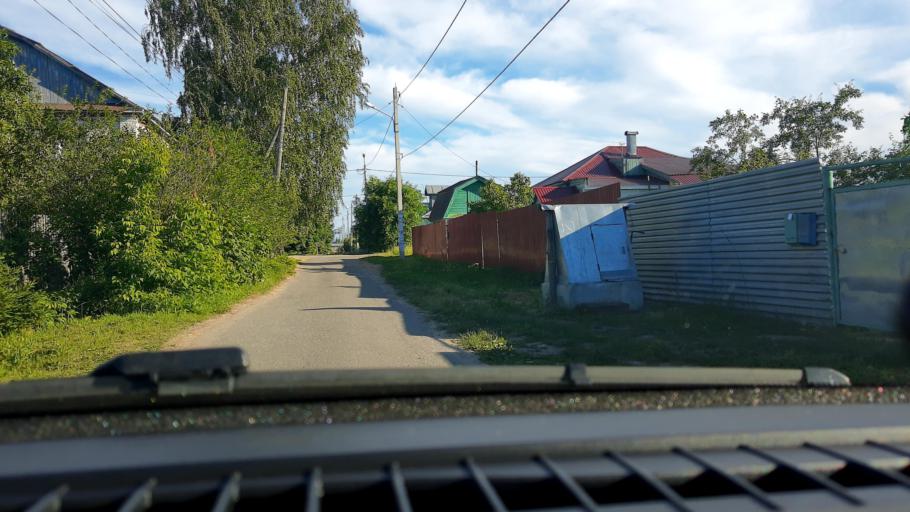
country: RU
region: Nizjnij Novgorod
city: Gorbatovka
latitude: 56.2692
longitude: 43.7687
